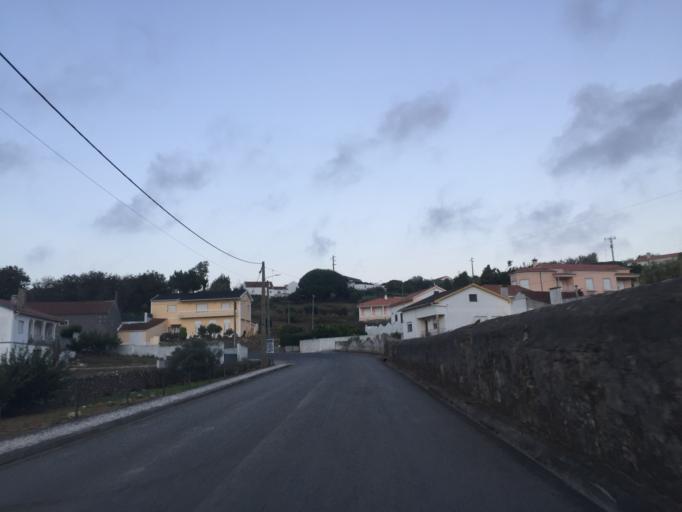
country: PT
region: Leiria
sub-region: Bombarral
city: Bombarral
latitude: 39.2860
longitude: -9.2154
